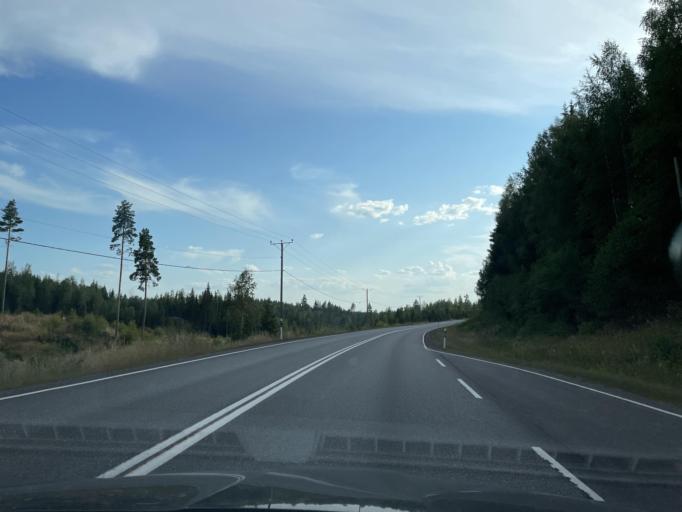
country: FI
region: Paijanne Tavastia
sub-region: Lahti
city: Auttoinen
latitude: 61.3222
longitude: 25.1631
